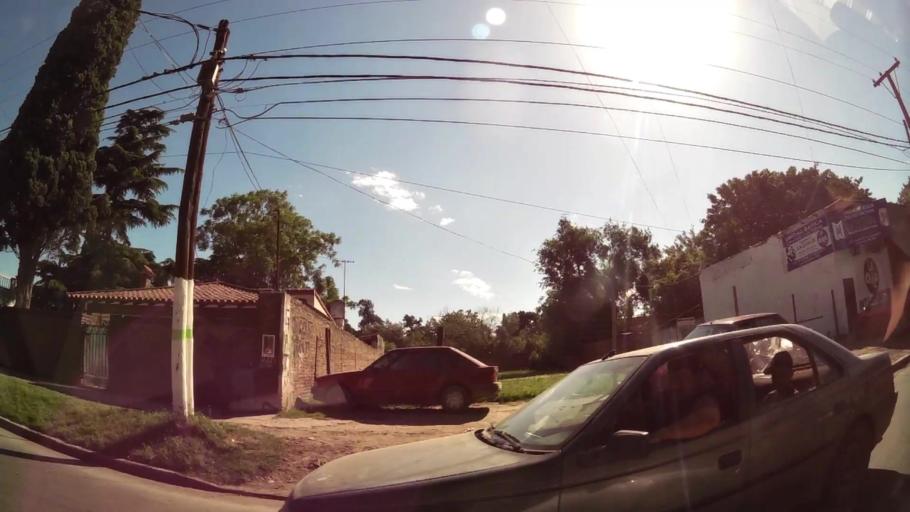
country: AR
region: Buenos Aires
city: Santa Catalina - Dique Lujan
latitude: -34.4813
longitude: -58.6998
